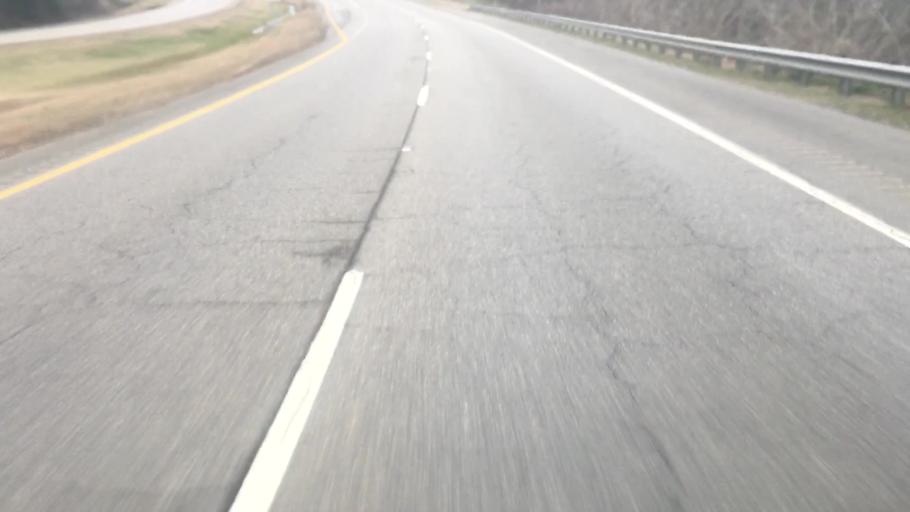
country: US
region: Alabama
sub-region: Walker County
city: Sumiton
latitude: 33.7490
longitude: -87.0569
